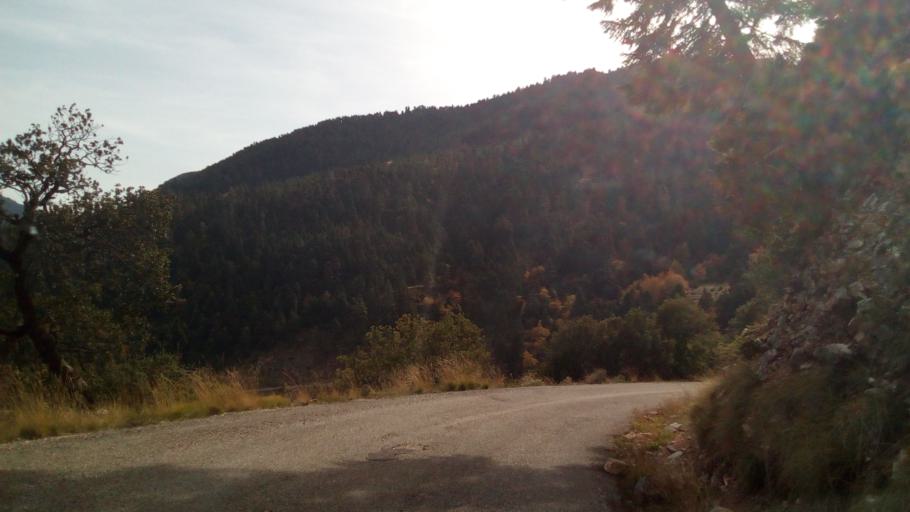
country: GR
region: West Greece
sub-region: Nomos Aitolias kai Akarnanias
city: Thermo
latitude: 38.5710
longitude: 21.8231
